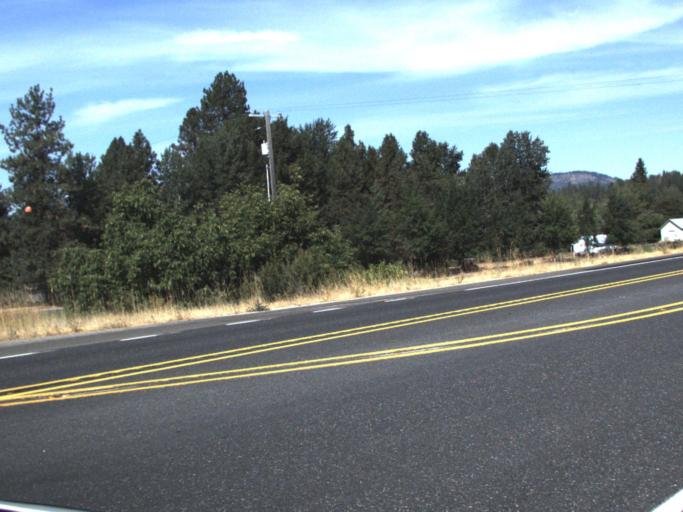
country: US
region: Washington
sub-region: Spokane County
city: Deer Park
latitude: 48.0382
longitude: -117.6052
